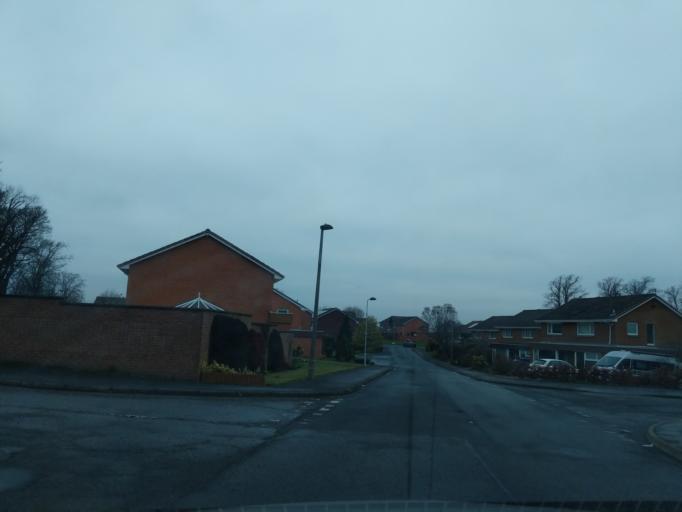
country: GB
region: Scotland
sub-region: Edinburgh
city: Balerno
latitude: 55.8916
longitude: -3.3338
